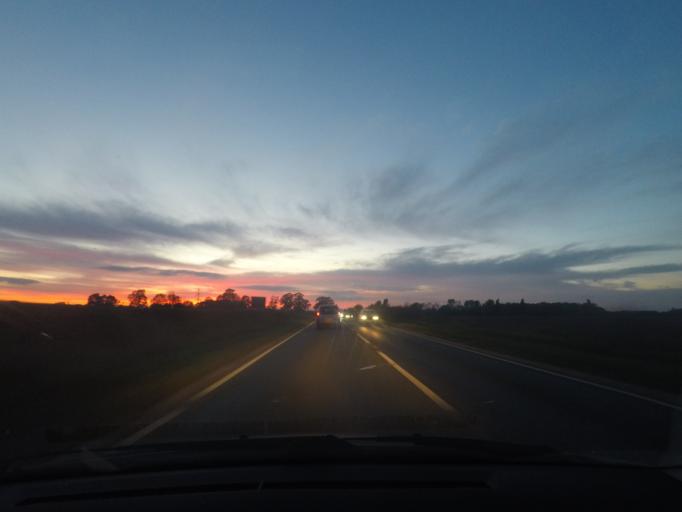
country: GB
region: England
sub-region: East Riding of Yorkshire
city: Wilberfoss
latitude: 53.9443
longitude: -0.8734
